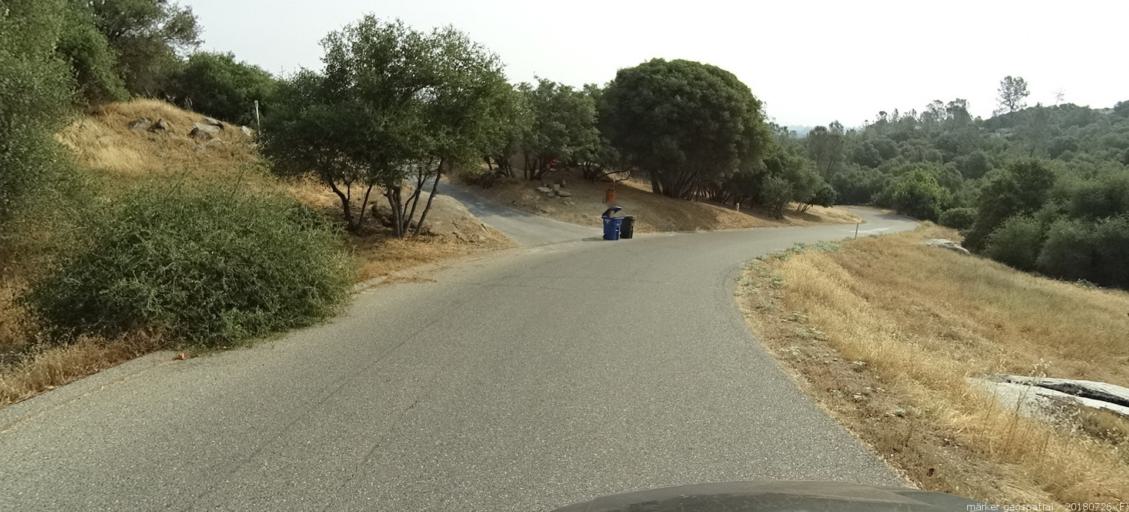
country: US
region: California
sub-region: Madera County
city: Coarsegold
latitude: 37.2011
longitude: -119.6866
